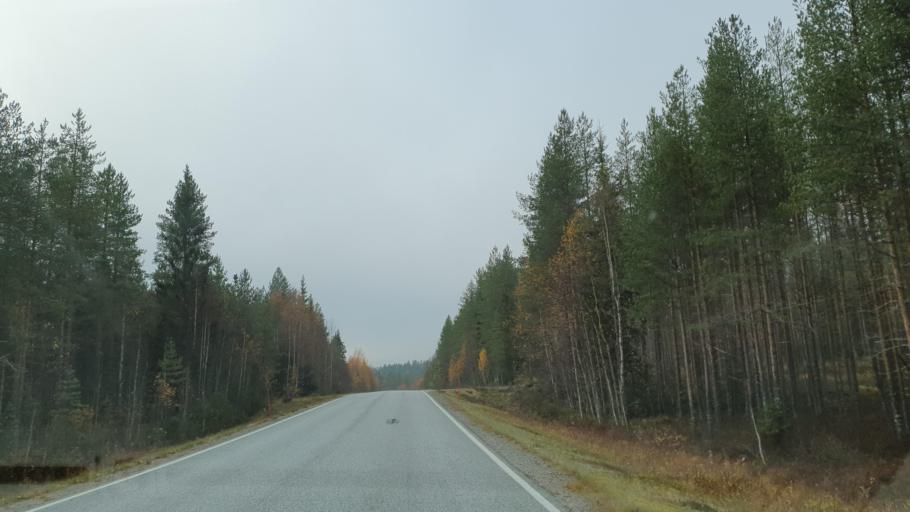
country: FI
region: Kainuu
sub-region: Kehys-Kainuu
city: Kuhmo
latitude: 64.4067
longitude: 29.4726
